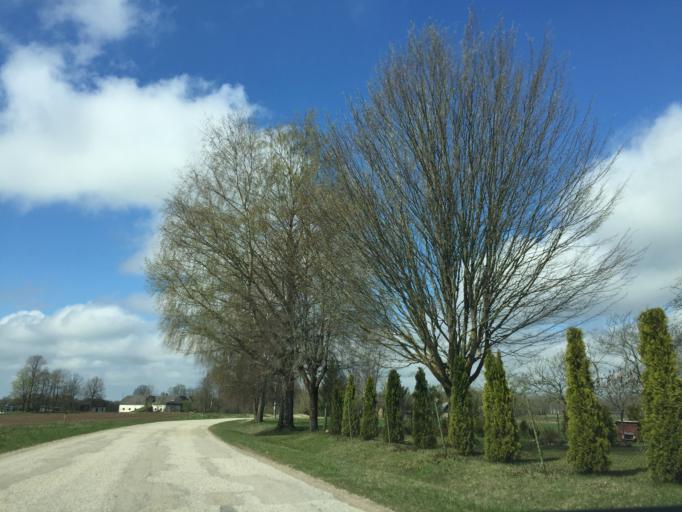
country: LV
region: Apes Novads
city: Ape
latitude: 57.4808
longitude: 26.4494
